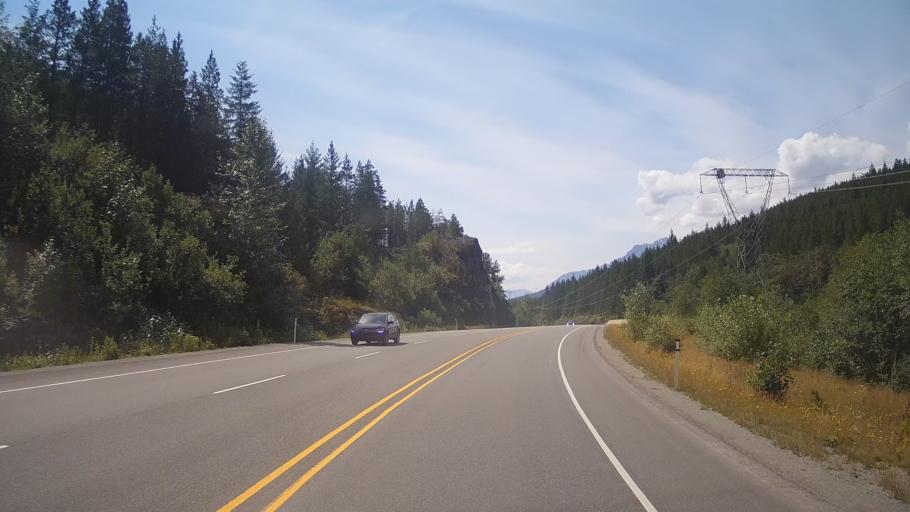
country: CA
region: British Columbia
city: Whistler
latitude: 49.8904
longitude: -123.1601
